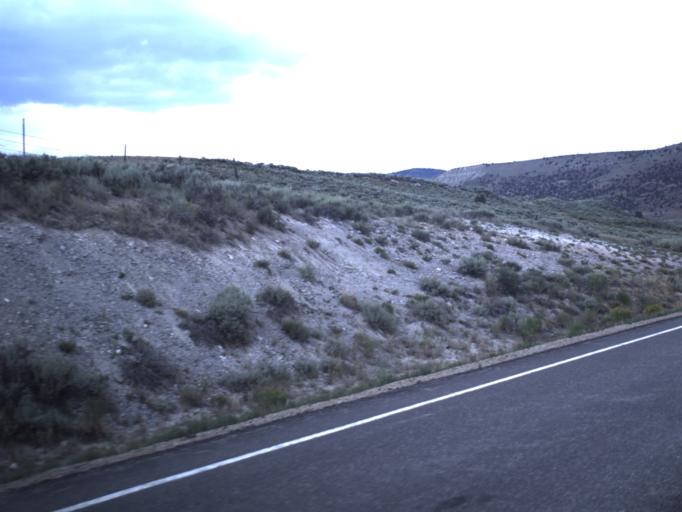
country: US
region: Utah
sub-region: Carbon County
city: Helper
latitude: 39.8034
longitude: -110.7816
